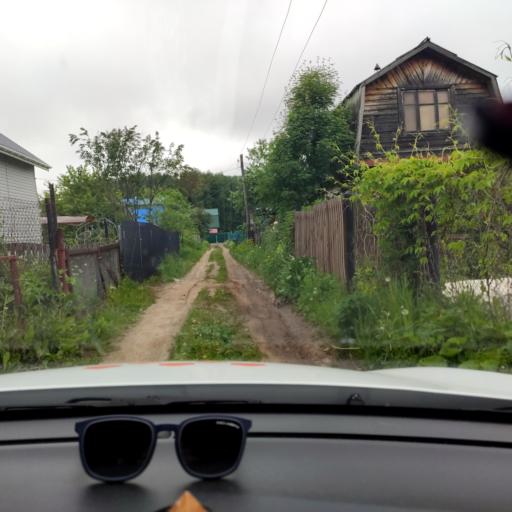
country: RU
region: Tatarstan
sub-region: Gorod Kazan'
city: Kazan
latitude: 55.9352
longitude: 49.0615
